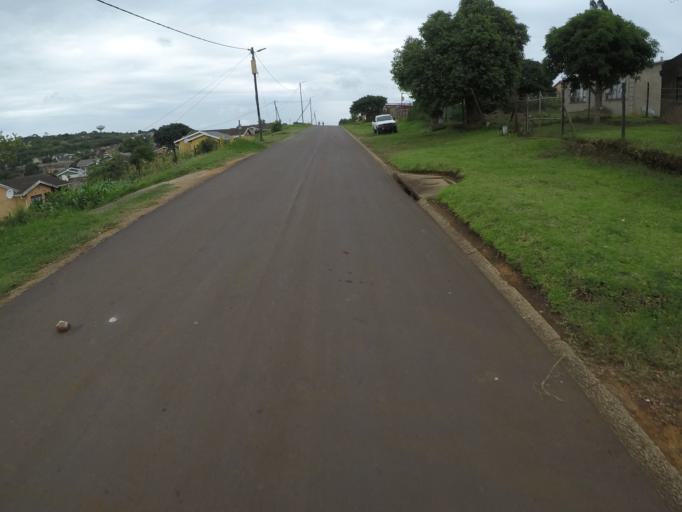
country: ZA
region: KwaZulu-Natal
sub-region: uThungulu District Municipality
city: Empangeni
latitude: -28.7705
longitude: 31.8702
